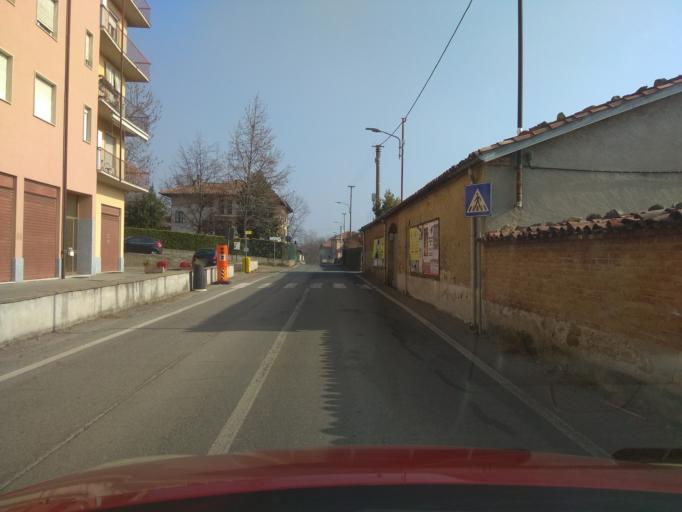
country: IT
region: Piedmont
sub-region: Provincia di Biella
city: Ronco Biellese
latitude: 45.5776
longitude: 8.0907
